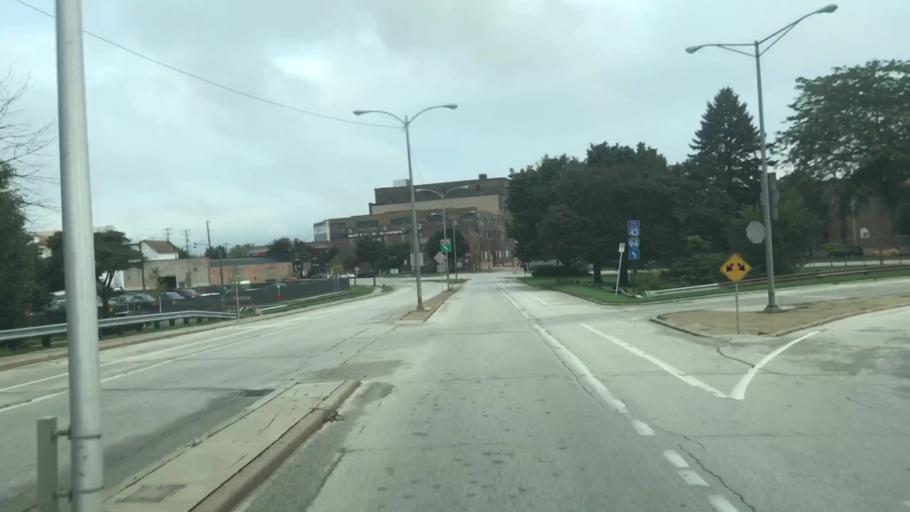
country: US
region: Wisconsin
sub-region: Milwaukee County
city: Milwaukee
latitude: 43.0038
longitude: -87.8975
